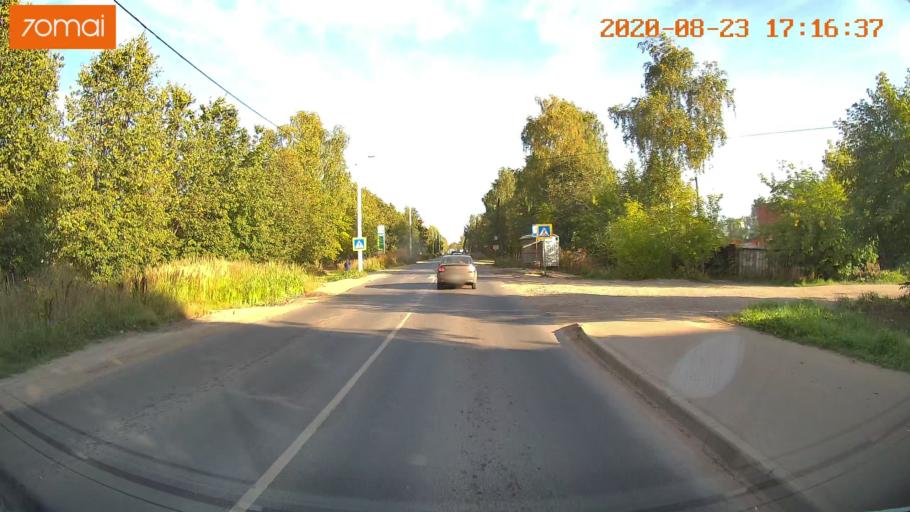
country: RU
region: Ivanovo
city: Novo-Talitsy
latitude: 57.0378
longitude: 40.9120
